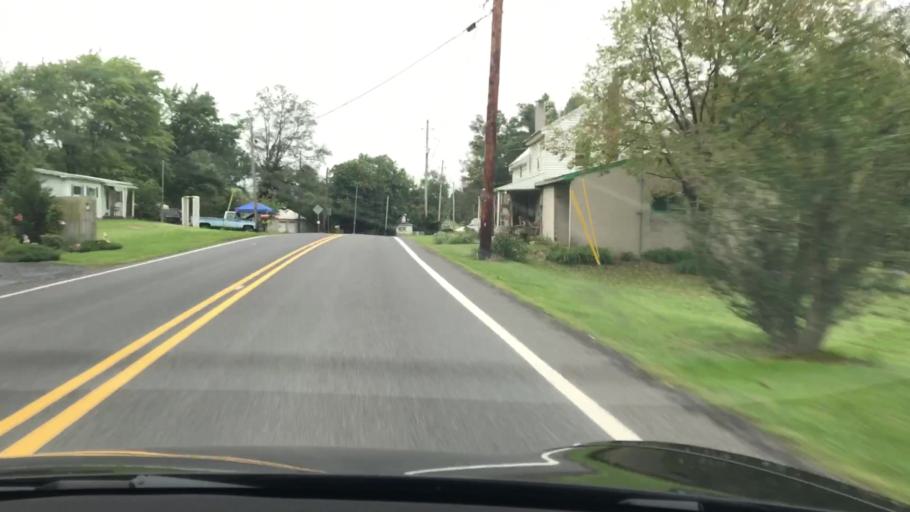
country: US
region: Pennsylvania
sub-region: Adams County
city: Lake Meade
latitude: 39.9506
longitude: -77.1155
